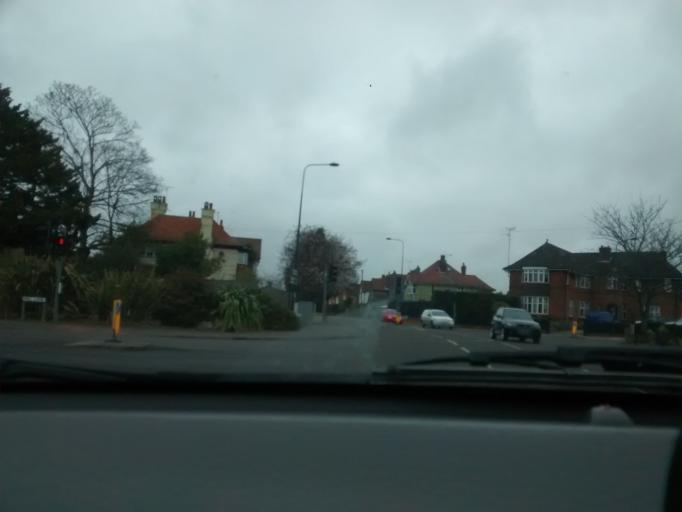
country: GB
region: England
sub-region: Suffolk
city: Felixstowe
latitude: 51.9624
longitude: 1.3436
